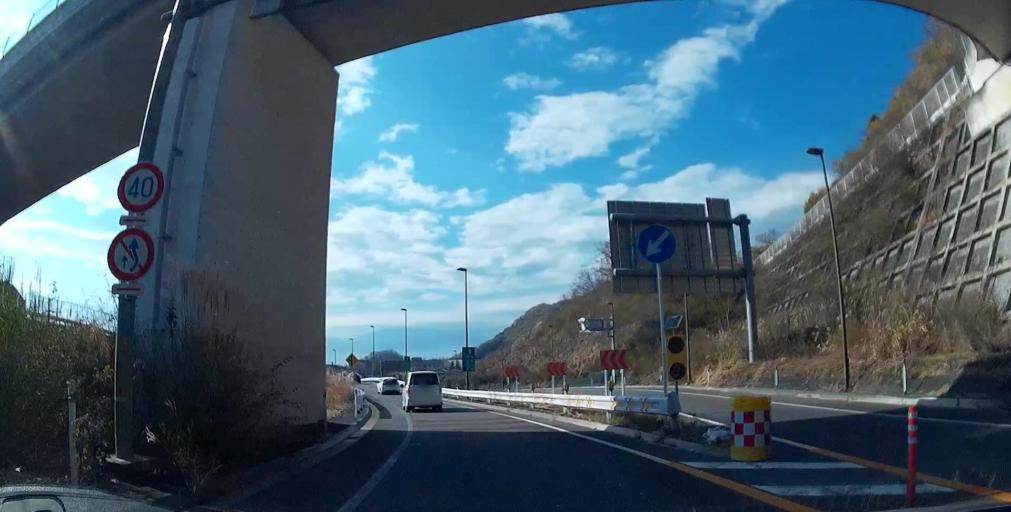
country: JP
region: Yamanashi
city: Isawa
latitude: 35.6630
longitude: 138.6185
